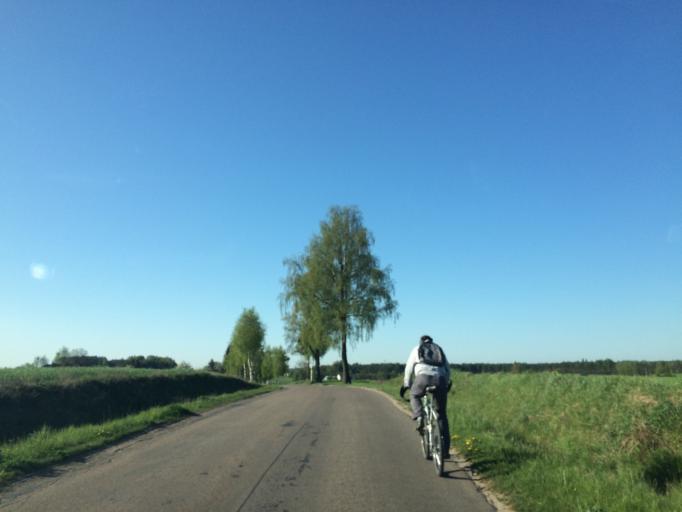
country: PL
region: Warmian-Masurian Voivodeship
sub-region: Powiat dzialdowski
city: Rybno
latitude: 53.4062
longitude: 19.9352
